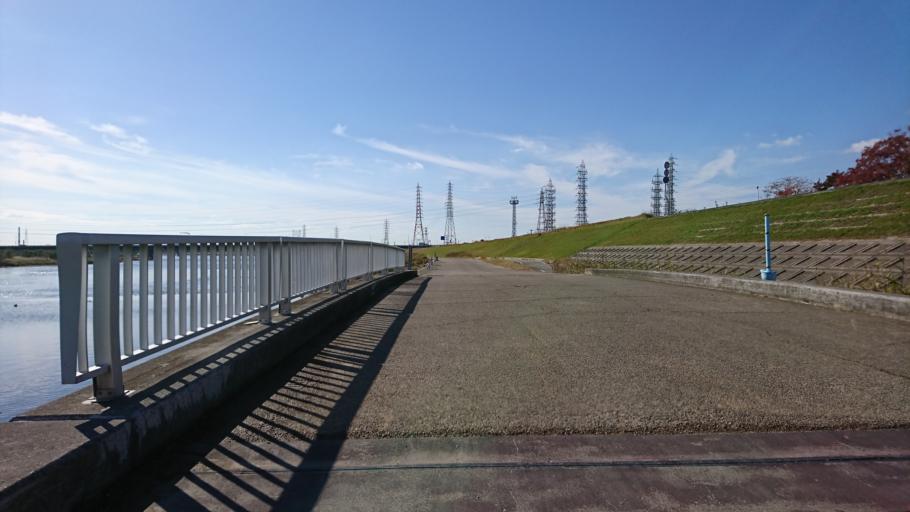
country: JP
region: Hyogo
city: Kakogawacho-honmachi
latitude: 34.7703
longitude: 134.8118
